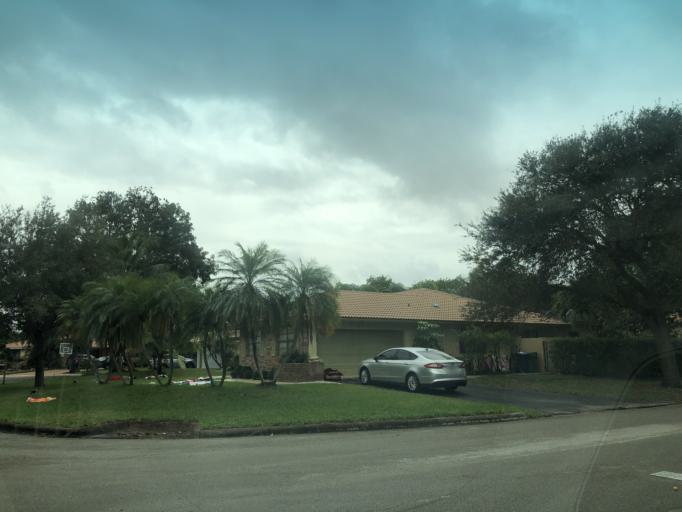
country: US
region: Florida
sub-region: Broward County
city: North Lauderdale
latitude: 26.2315
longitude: -80.2378
